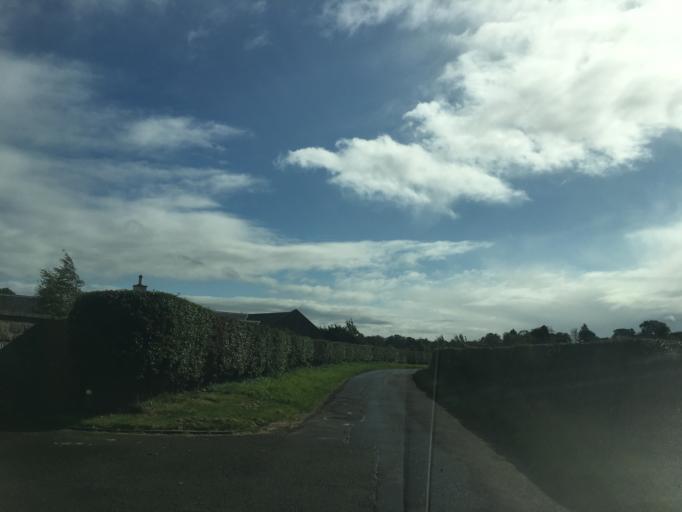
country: GB
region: Scotland
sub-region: Edinburgh
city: Kirkliston
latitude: 55.9603
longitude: -3.3743
